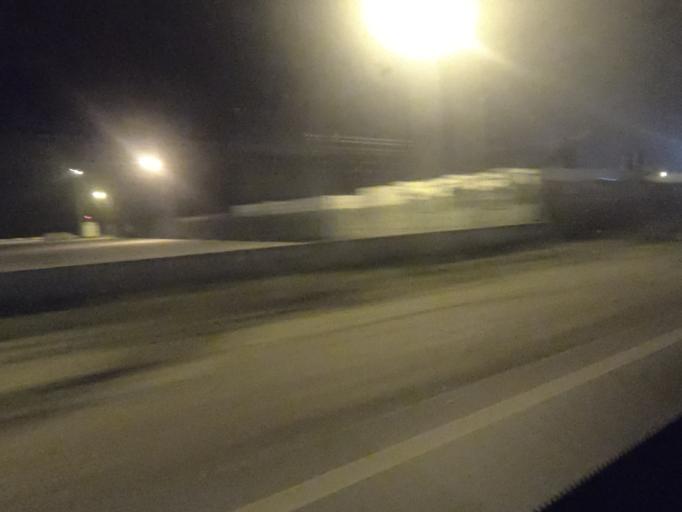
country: PT
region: Setubal
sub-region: Setubal
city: Setubal
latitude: 38.5092
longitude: -8.8515
